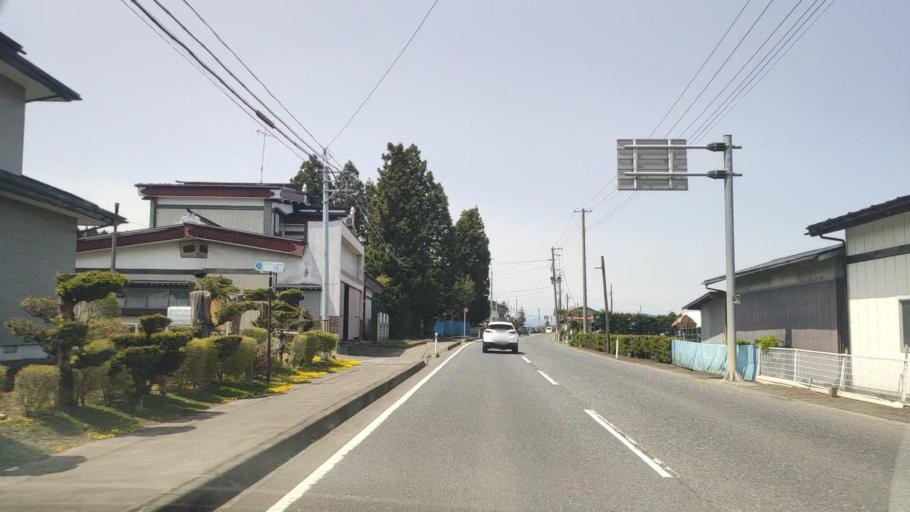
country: JP
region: Aomori
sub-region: Misawa Shi
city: Inuotose
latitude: 40.5915
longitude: 141.3481
